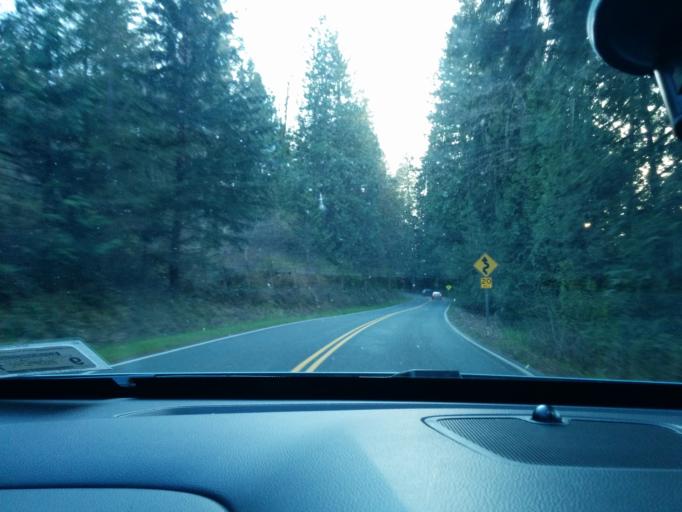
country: US
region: Washington
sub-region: Snohomish County
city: Sultan
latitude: 47.9018
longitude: -121.7817
